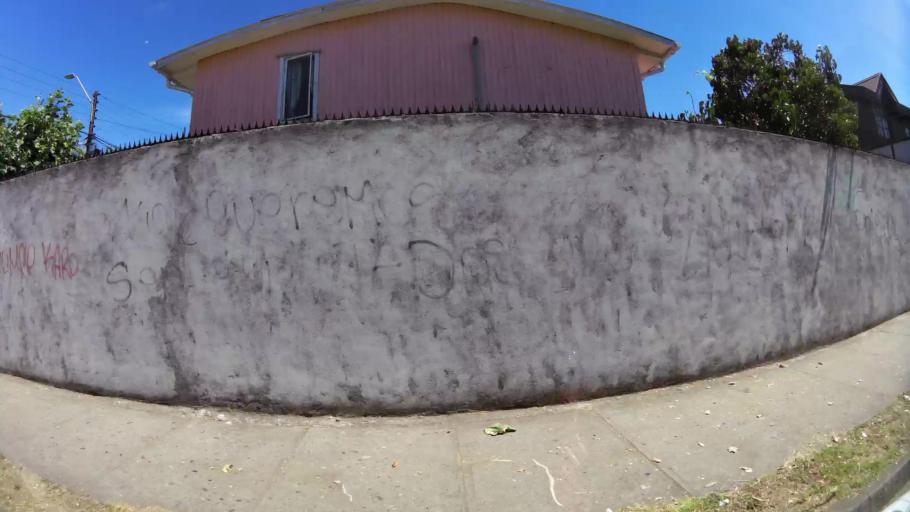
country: CL
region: Biobio
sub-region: Provincia de Concepcion
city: Talcahuano
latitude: -36.7613
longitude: -73.0873
